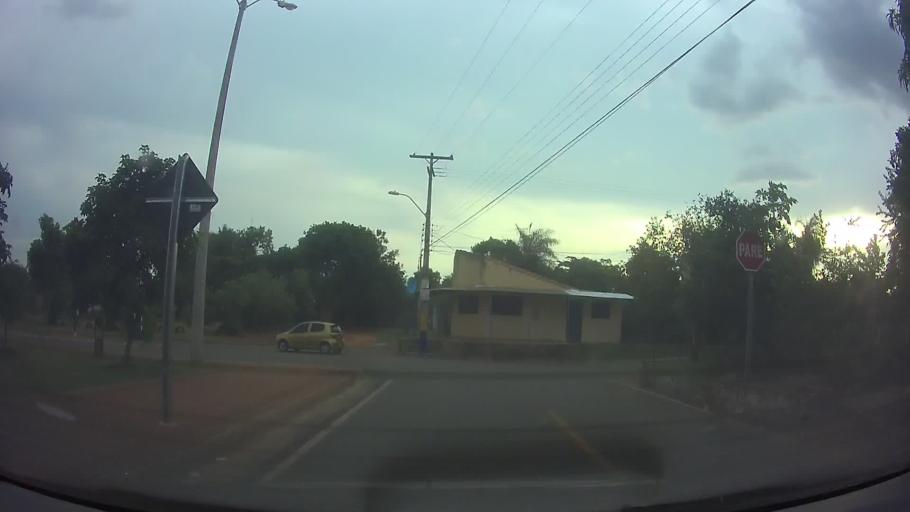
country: PY
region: Central
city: San Lorenzo
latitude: -25.2737
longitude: -57.4667
